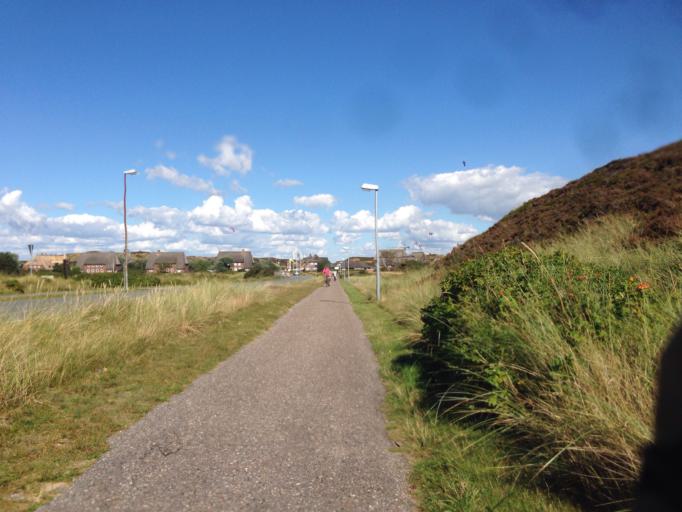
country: DE
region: Schleswig-Holstein
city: List
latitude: 55.0109
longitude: 8.4170
